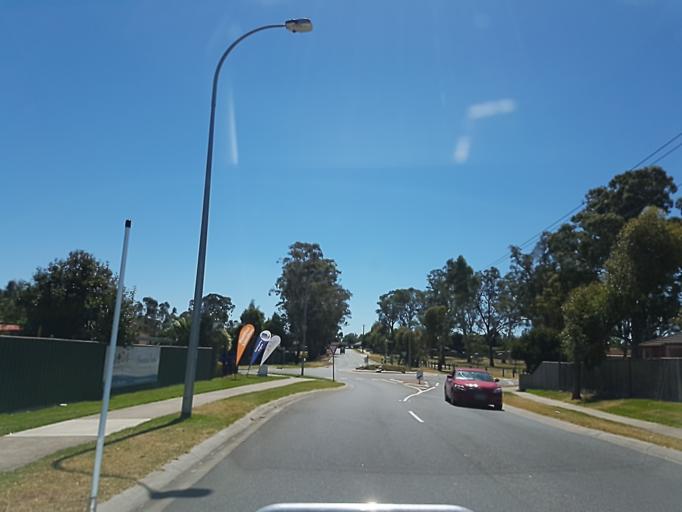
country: AU
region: Victoria
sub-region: Casey
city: Hampton Park
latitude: -38.0414
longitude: 145.2532
